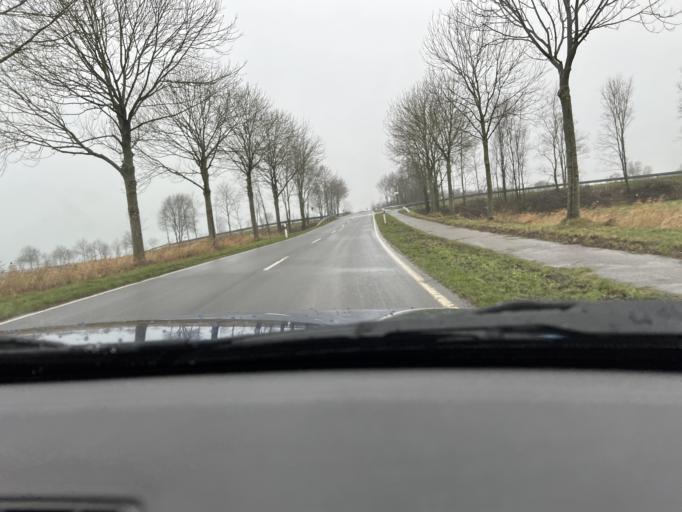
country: DE
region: Schleswig-Holstein
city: Stelle-Wittenwurth
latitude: 54.2417
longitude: 9.0412
